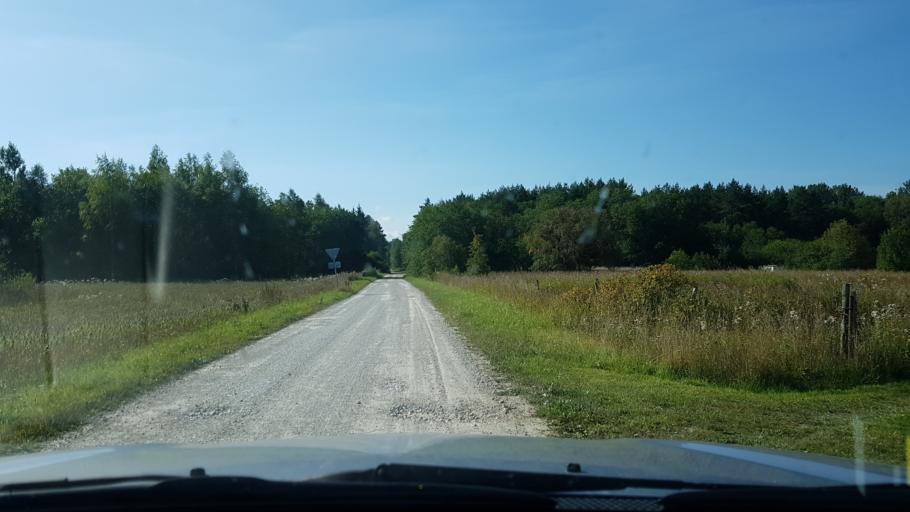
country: EE
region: Ida-Virumaa
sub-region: Toila vald
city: Voka
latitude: 59.3911
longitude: 27.6675
